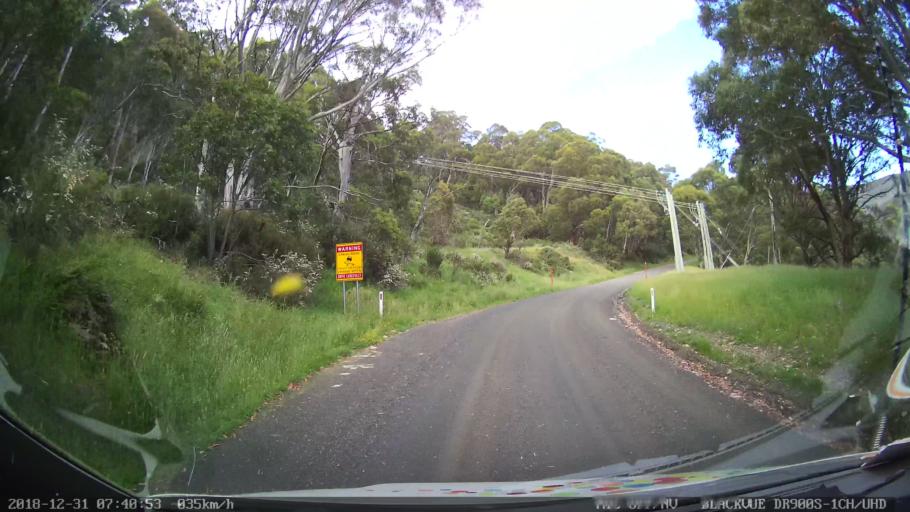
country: AU
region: New South Wales
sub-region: Snowy River
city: Jindabyne
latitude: -36.3527
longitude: 148.4153
